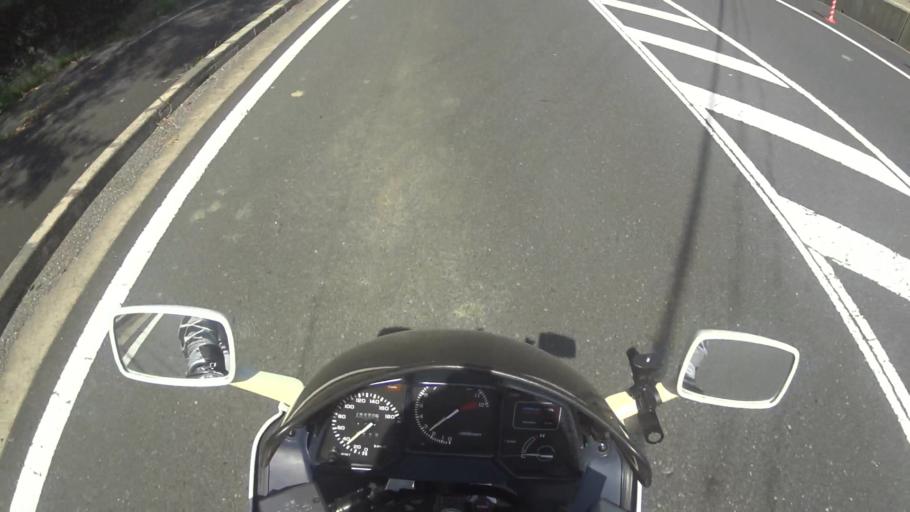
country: JP
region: Kyoto
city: Miyazu
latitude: 35.7301
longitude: 135.2558
